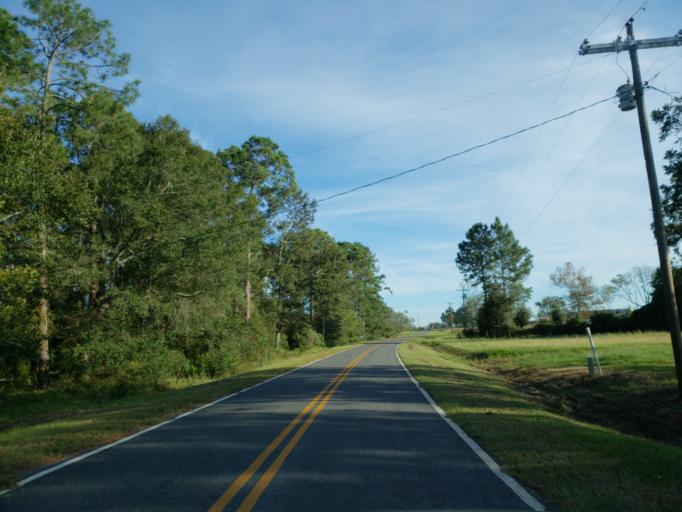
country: US
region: Georgia
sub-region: Dooly County
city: Vienna
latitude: 32.0455
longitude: -83.7561
